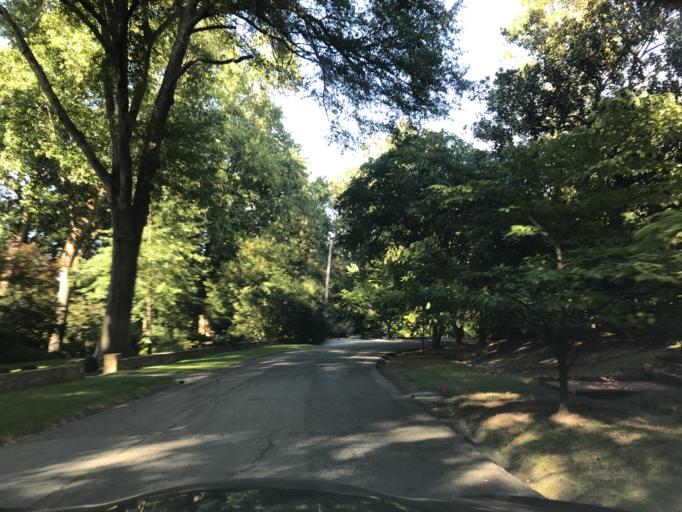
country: US
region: North Carolina
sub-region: Orange County
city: Chapel Hill
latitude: 35.9214
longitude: -79.0447
